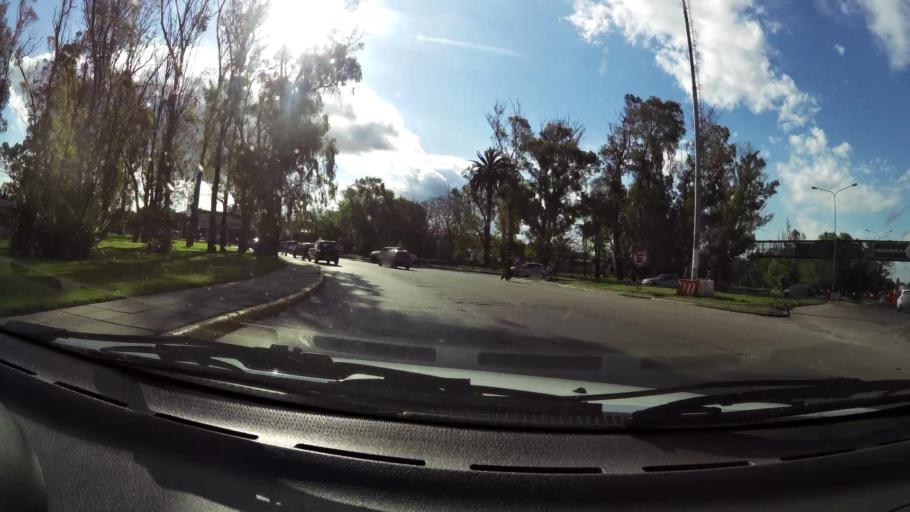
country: AR
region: Buenos Aires
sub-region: Partido de La Plata
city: La Plata
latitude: -34.8881
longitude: -57.9565
